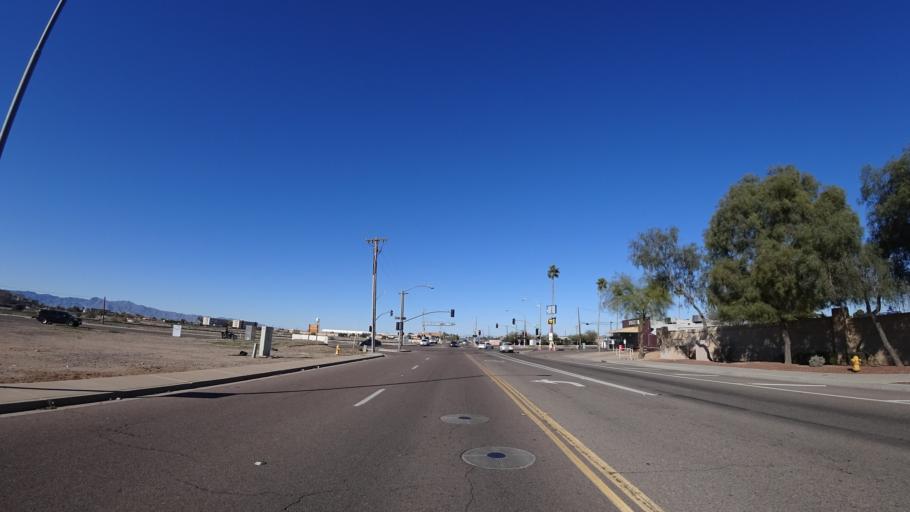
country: US
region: Arizona
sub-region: Maricopa County
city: Goodyear
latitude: 33.4241
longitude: -112.3579
